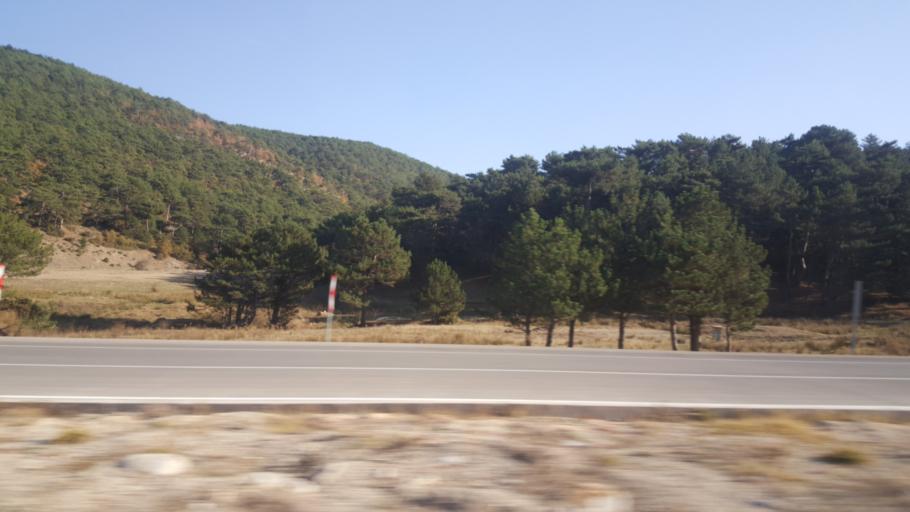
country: TR
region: Afyonkarahisar
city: Ihsaniye
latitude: 39.0999
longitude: 30.5779
